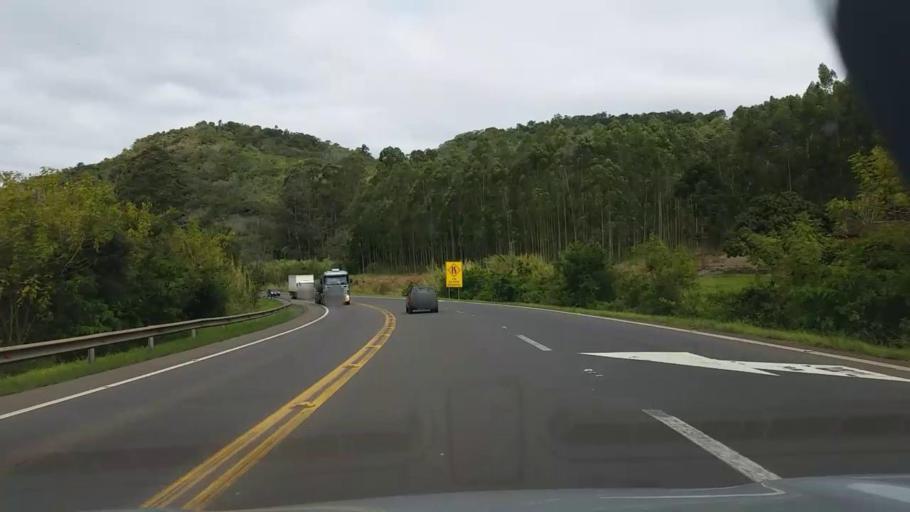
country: BR
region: Rio Grande do Sul
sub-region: Arroio Do Meio
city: Arroio do Meio
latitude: -29.3831
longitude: -52.0544
